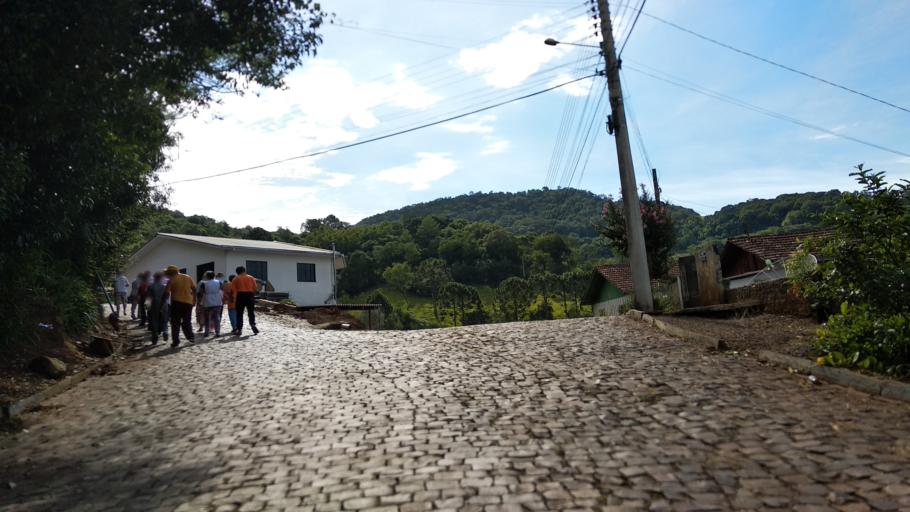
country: BR
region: Santa Catarina
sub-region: Videira
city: Videira
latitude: -27.1011
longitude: -51.2383
